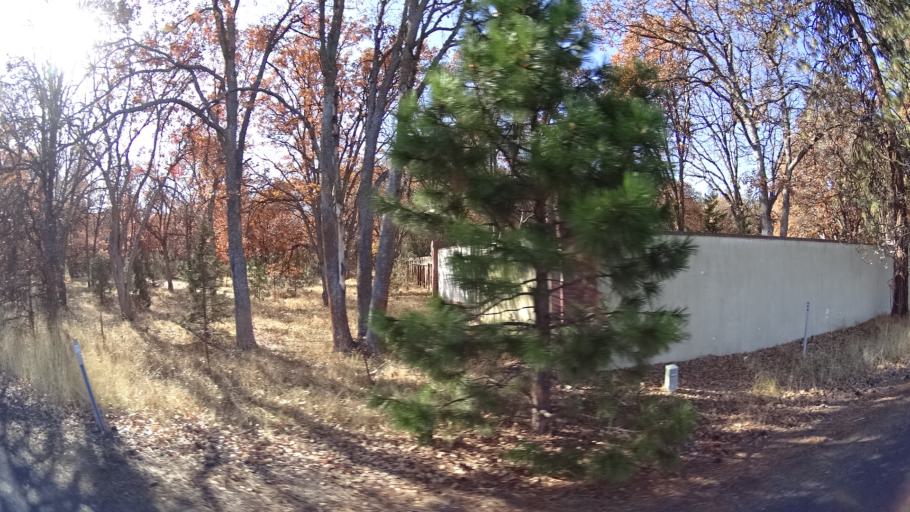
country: US
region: California
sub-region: Siskiyou County
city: Yreka
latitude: 41.6627
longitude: -122.6019
